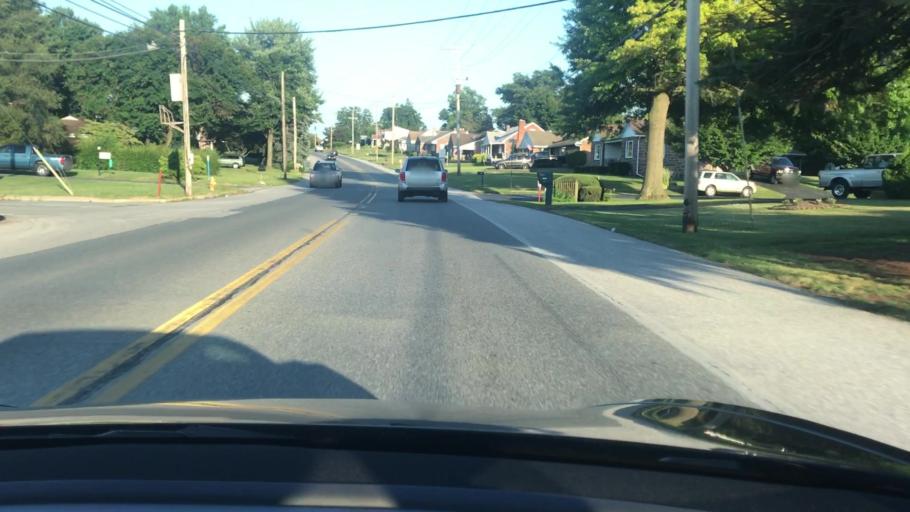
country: US
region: Pennsylvania
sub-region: York County
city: Weigelstown
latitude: 39.9858
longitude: -76.8296
